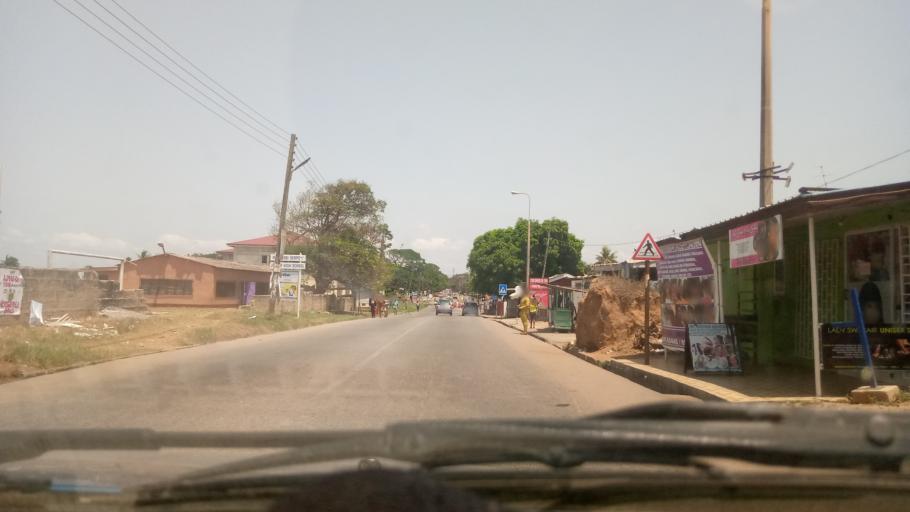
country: GH
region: Greater Accra
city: Accra
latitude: 5.5369
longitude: -0.2383
